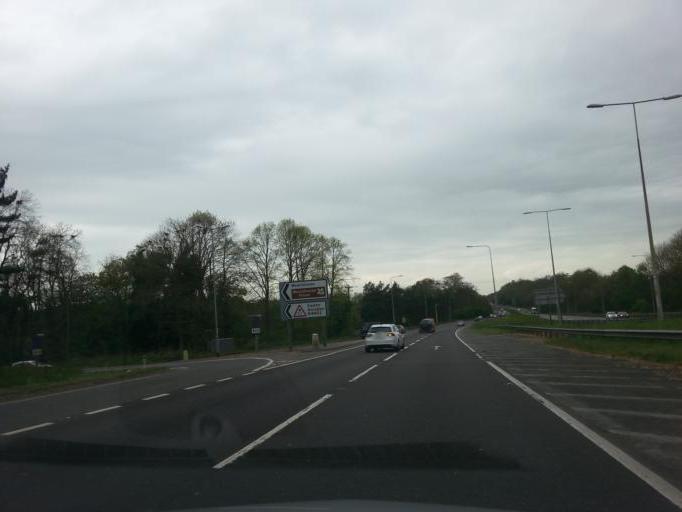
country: GB
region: England
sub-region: District of Rutland
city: Greetham
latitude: 52.8147
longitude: -0.6212
